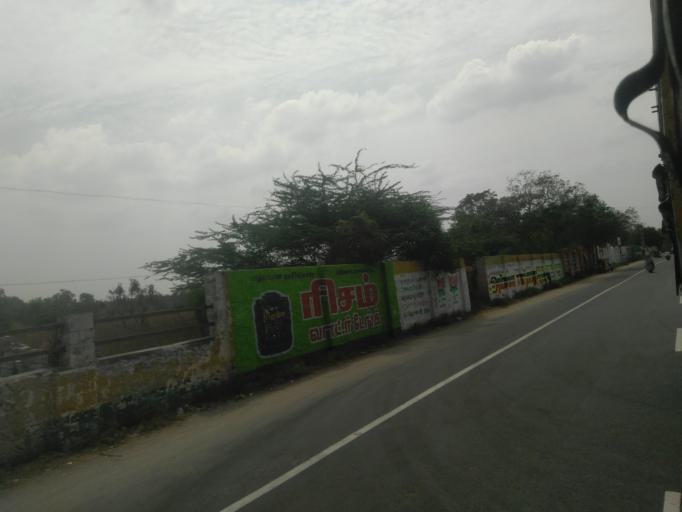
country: IN
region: Tamil Nadu
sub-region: Coimbatore
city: Irugur
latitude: 11.0025
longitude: 77.0608
